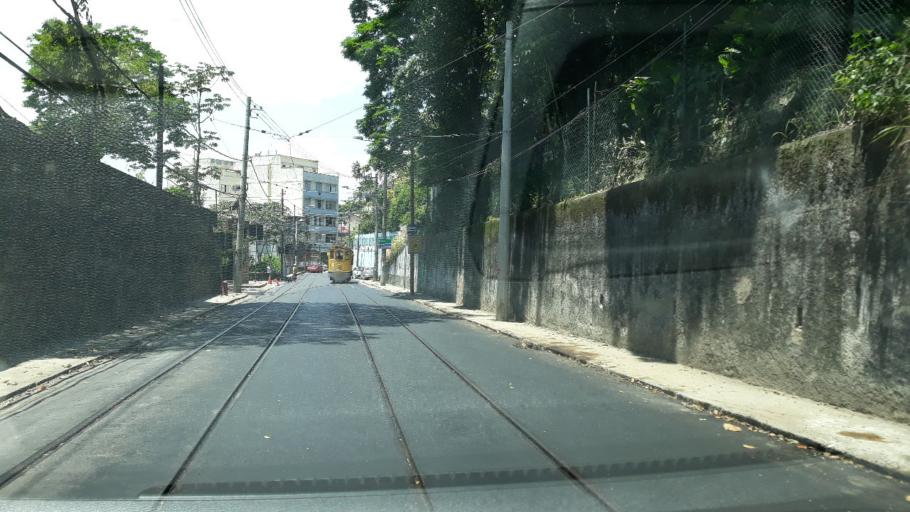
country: BR
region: Rio de Janeiro
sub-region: Rio De Janeiro
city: Rio de Janeiro
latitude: -22.9303
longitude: -43.1958
